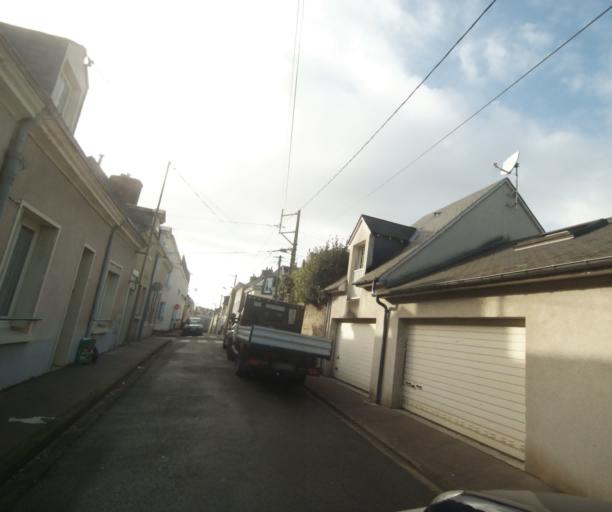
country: FR
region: Pays de la Loire
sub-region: Departement de la Sarthe
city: Le Mans
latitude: 47.9981
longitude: 0.1973
